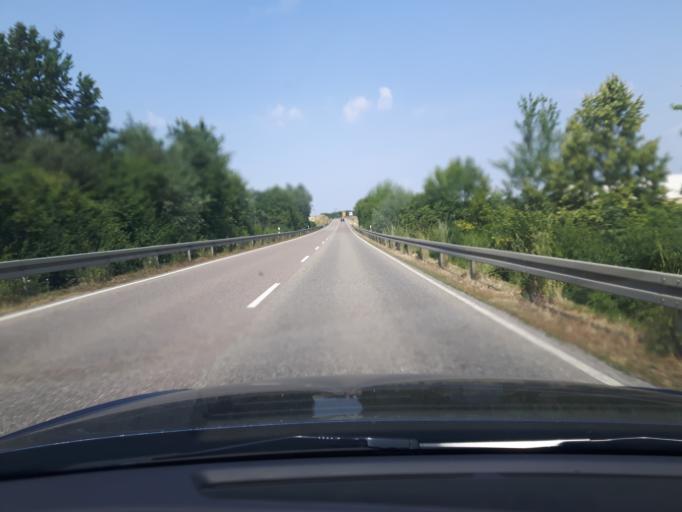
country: DE
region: Baden-Wuerttemberg
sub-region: Regierungsbezirk Stuttgart
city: Eppingen
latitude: 49.1437
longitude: 8.9258
